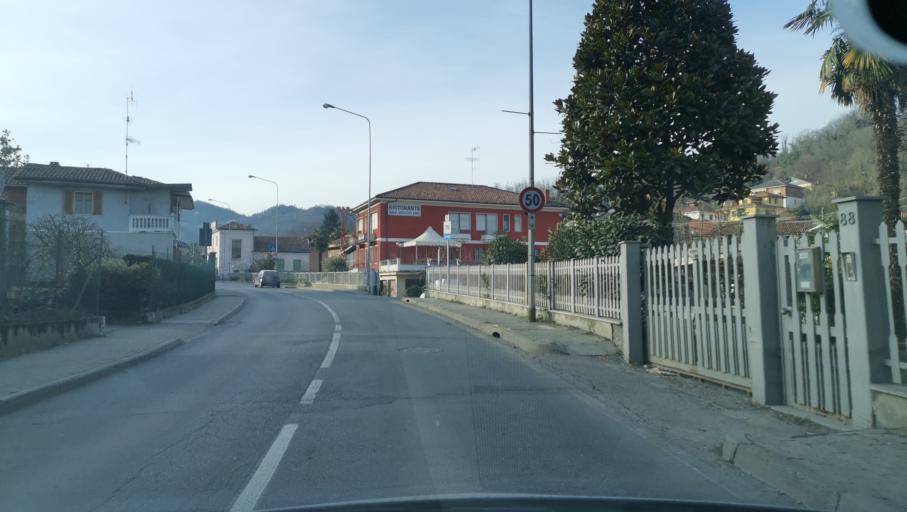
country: IT
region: Piedmont
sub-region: Provincia di Torino
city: Castiglione Torinese
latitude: 45.1150
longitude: 7.8166
